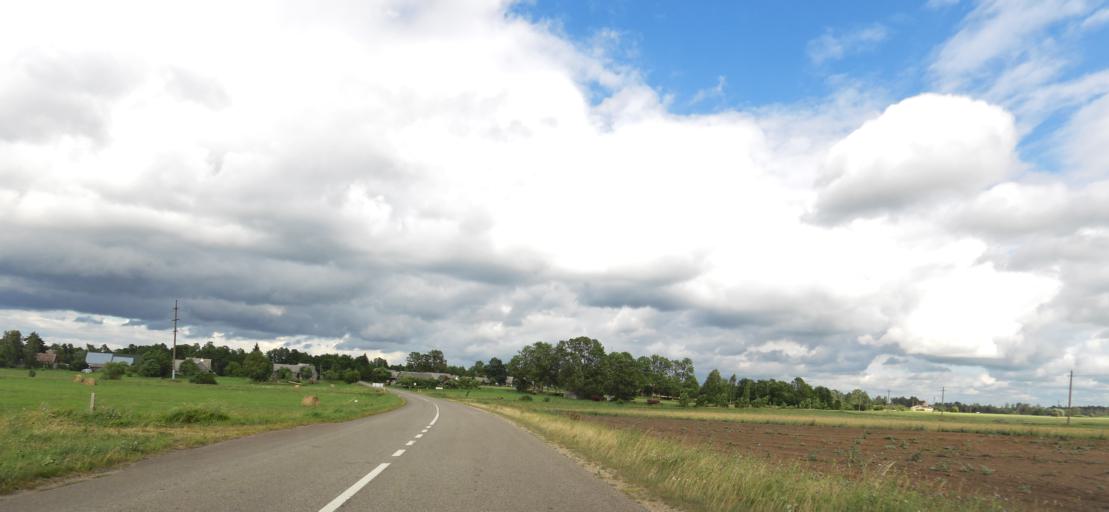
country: LT
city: Obeliai
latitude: 55.8900
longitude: 25.1903
